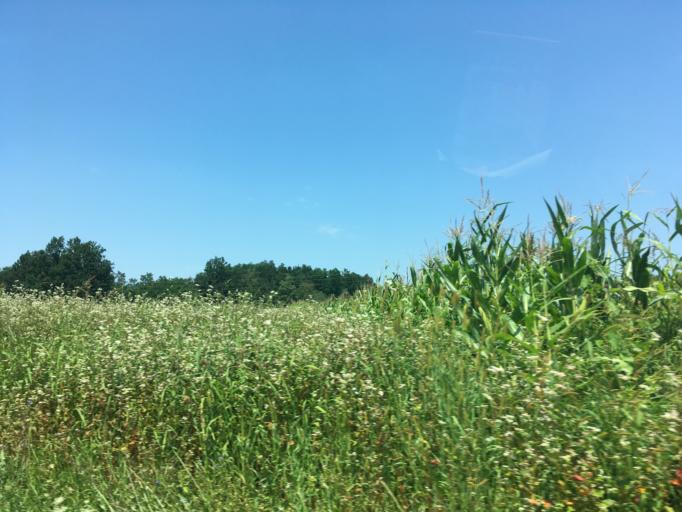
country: SI
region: Metlika
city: Metlika
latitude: 45.6484
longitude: 15.3588
